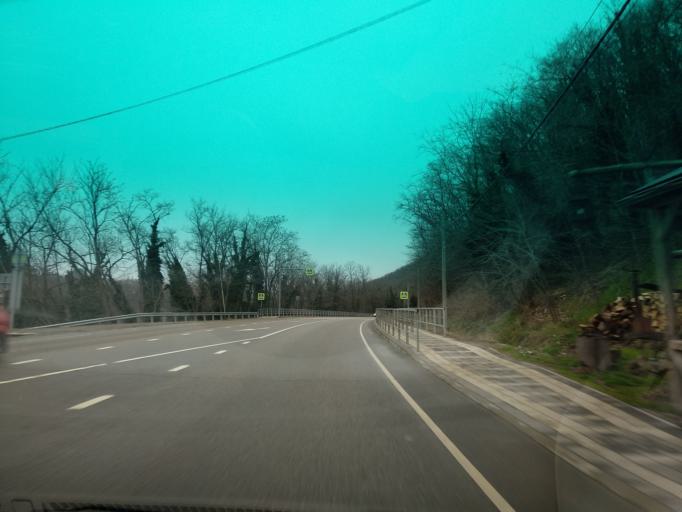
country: RU
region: Krasnodarskiy
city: Tuapse
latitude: 44.1068
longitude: 39.0745
